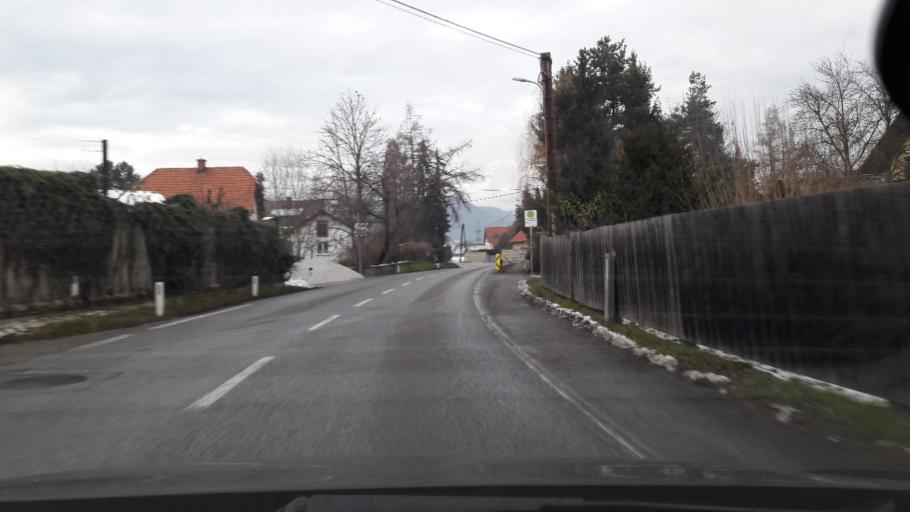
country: AT
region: Styria
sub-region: Politischer Bezirk Graz-Umgebung
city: Gratkorn
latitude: 47.1200
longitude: 15.3366
